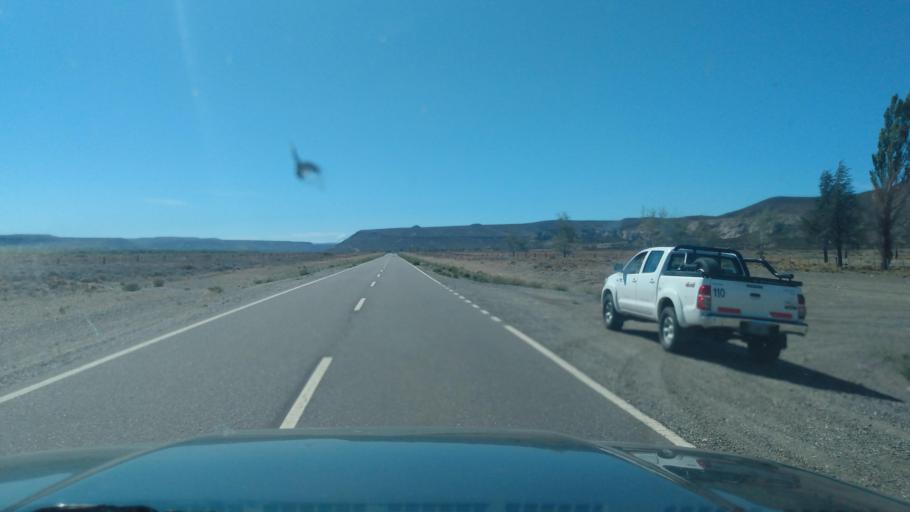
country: AR
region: Neuquen
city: Junin de los Andes
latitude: -40.1486
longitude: -70.7003
